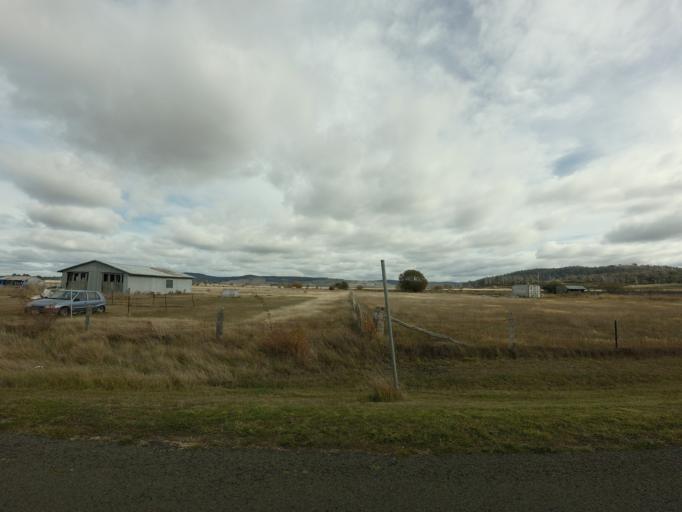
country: AU
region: Tasmania
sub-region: Brighton
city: Bridgewater
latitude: -42.4032
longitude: 147.3917
